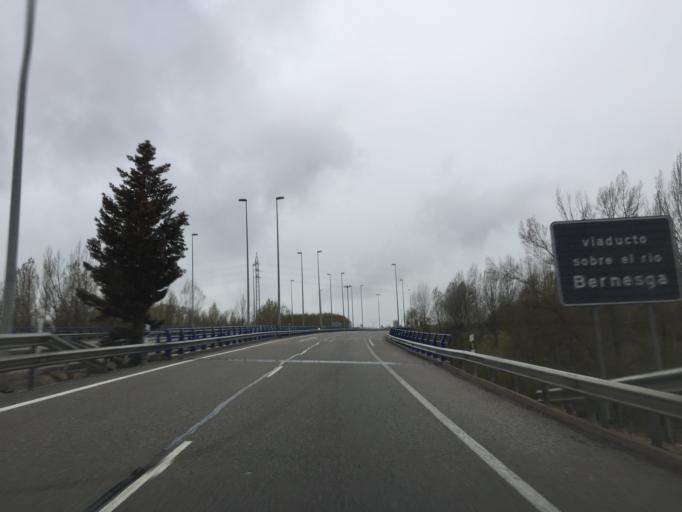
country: ES
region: Castille and Leon
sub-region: Provincia de Leon
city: Leon
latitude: 42.5721
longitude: -5.5651
